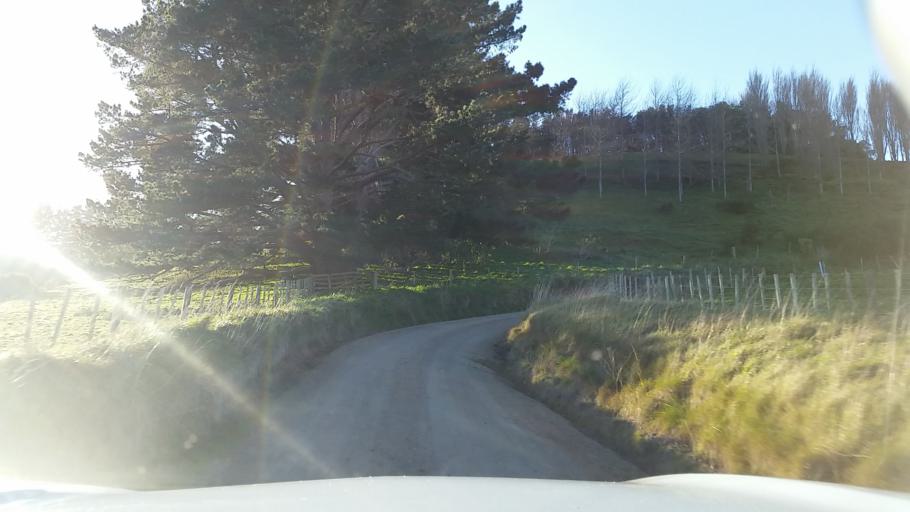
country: NZ
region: Taranaki
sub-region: South Taranaki District
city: Patea
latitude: -39.7548
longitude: 174.7462
